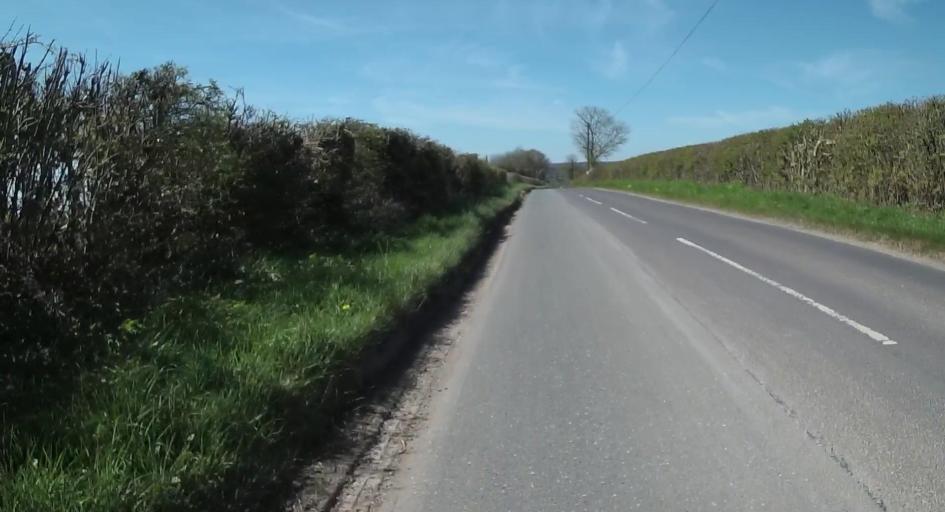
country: GB
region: England
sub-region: Hampshire
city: Winchester
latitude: 51.1029
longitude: -1.3708
